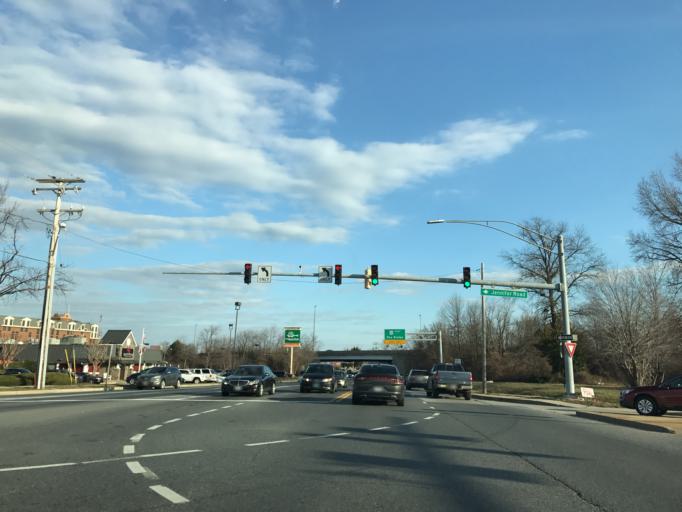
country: US
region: Maryland
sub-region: Anne Arundel County
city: Parole
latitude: 38.9851
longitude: -76.5457
